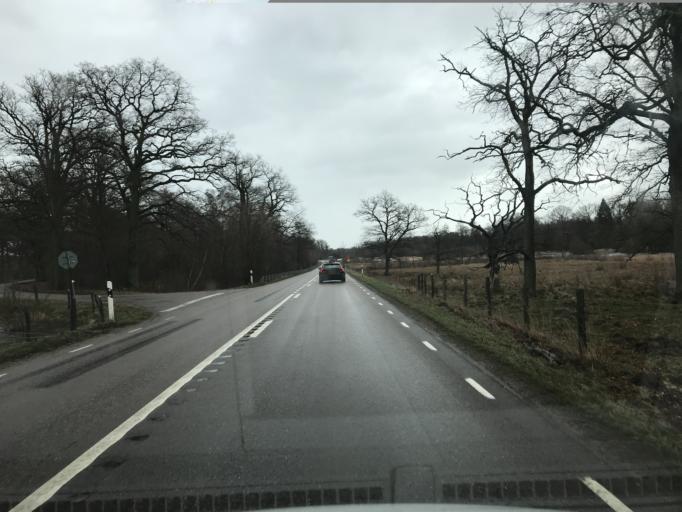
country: SE
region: Skane
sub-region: Klippans Kommun
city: Ljungbyhed
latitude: 56.0910
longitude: 13.2223
